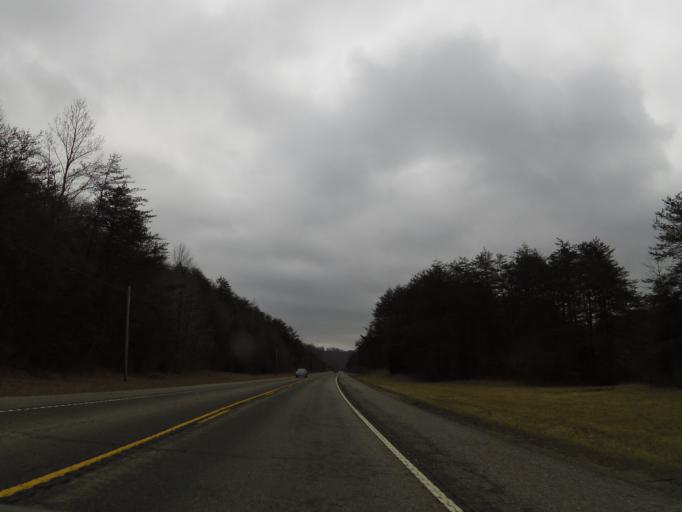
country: US
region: Tennessee
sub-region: Campbell County
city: Caryville
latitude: 36.4013
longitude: -84.2844
